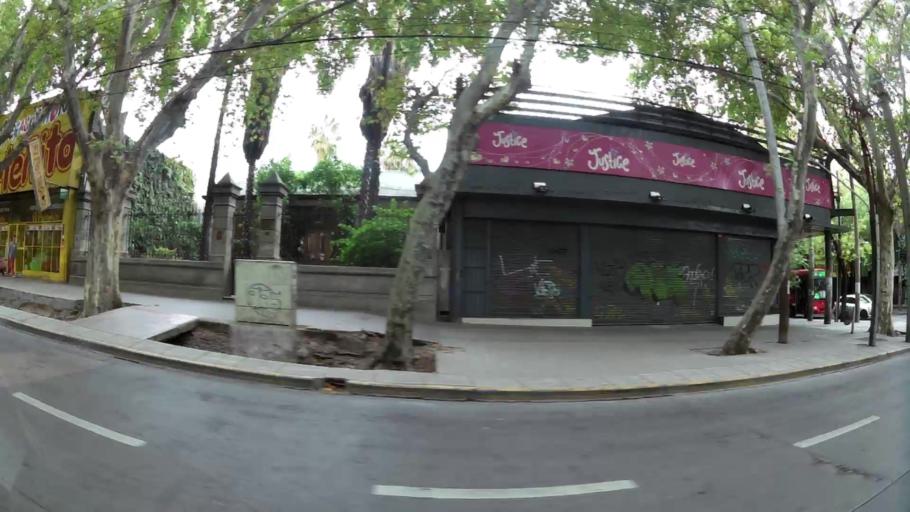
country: AR
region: Mendoza
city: Mendoza
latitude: -32.8837
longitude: -68.8392
